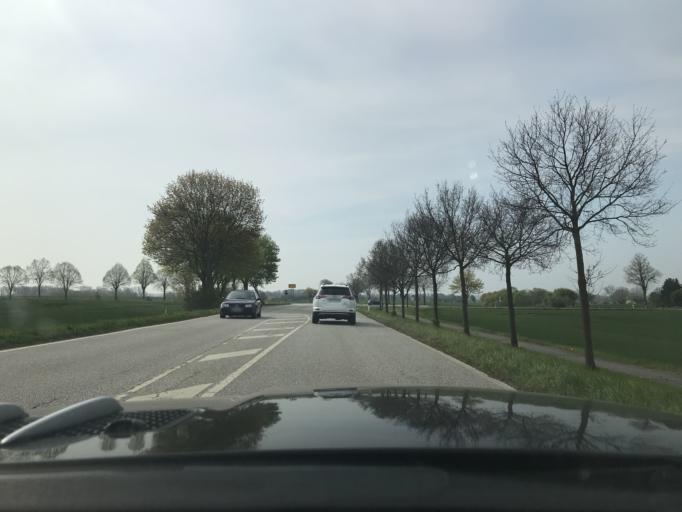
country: DE
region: Schleswig-Holstein
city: Grube
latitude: 54.2667
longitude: 11.0338
